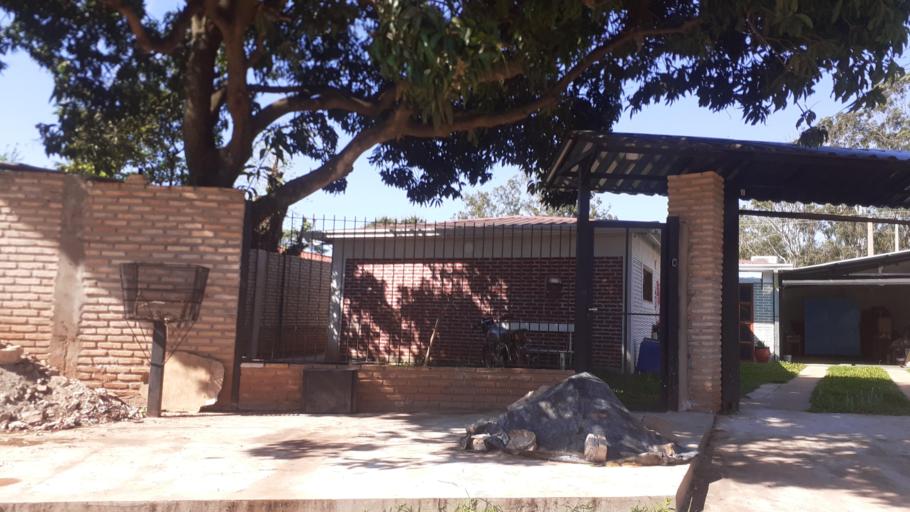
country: PY
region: Misiones
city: San Juan Bautista
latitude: -26.6662
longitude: -57.1305
